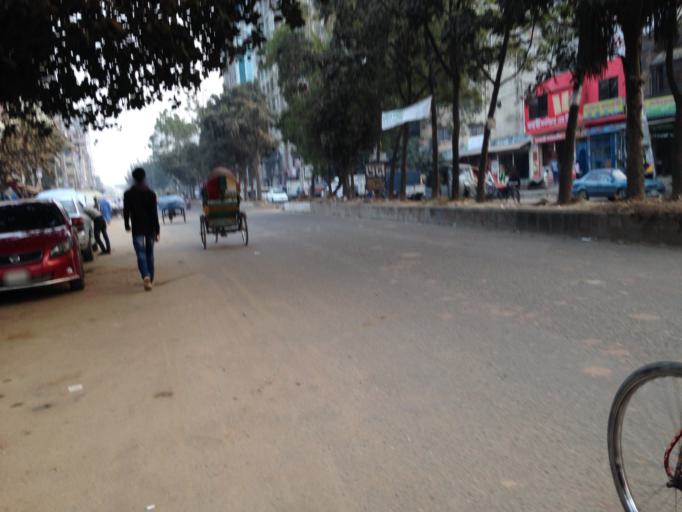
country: BD
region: Dhaka
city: Azimpur
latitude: 23.8043
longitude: 90.3524
